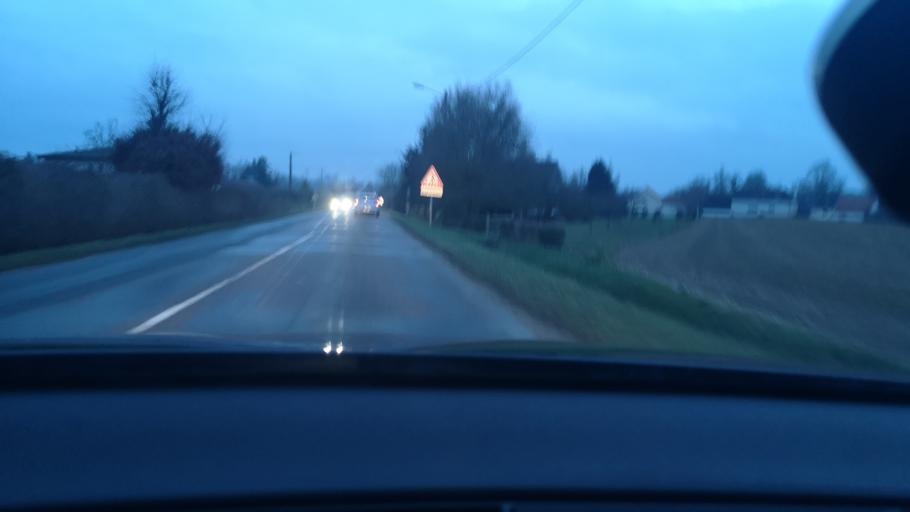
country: FR
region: Bourgogne
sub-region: Departement de Saone-et-Loire
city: Demigny
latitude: 46.9546
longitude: 4.9068
